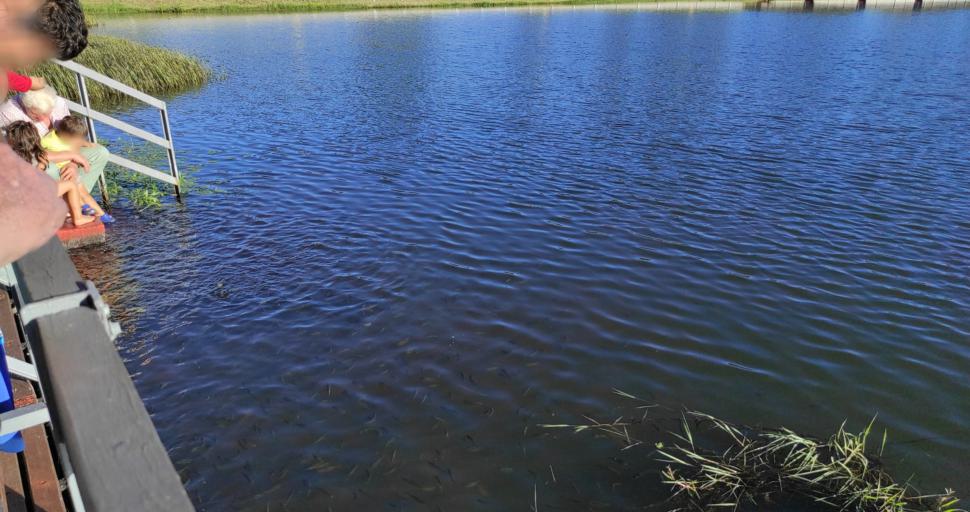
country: AR
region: Misiones
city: Dos de Mayo
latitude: -27.0411
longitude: -54.6801
